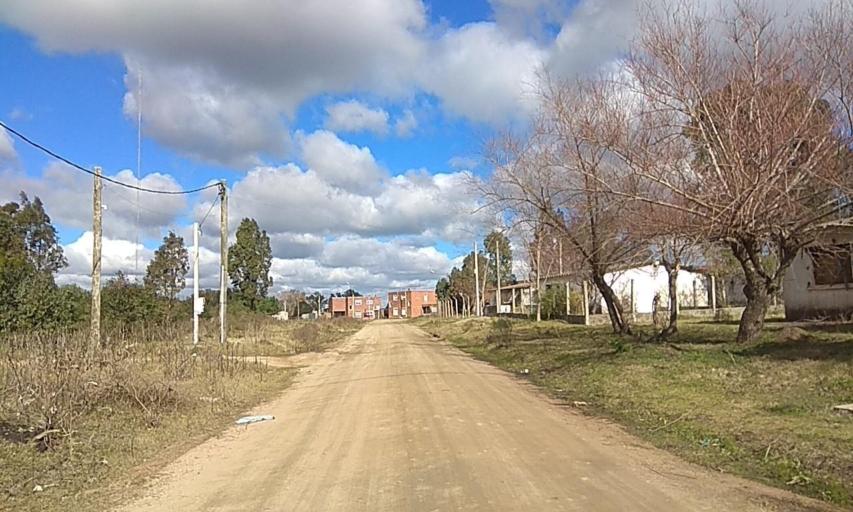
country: UY
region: Florida
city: Florida
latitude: -34.0957
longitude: -56.2326
